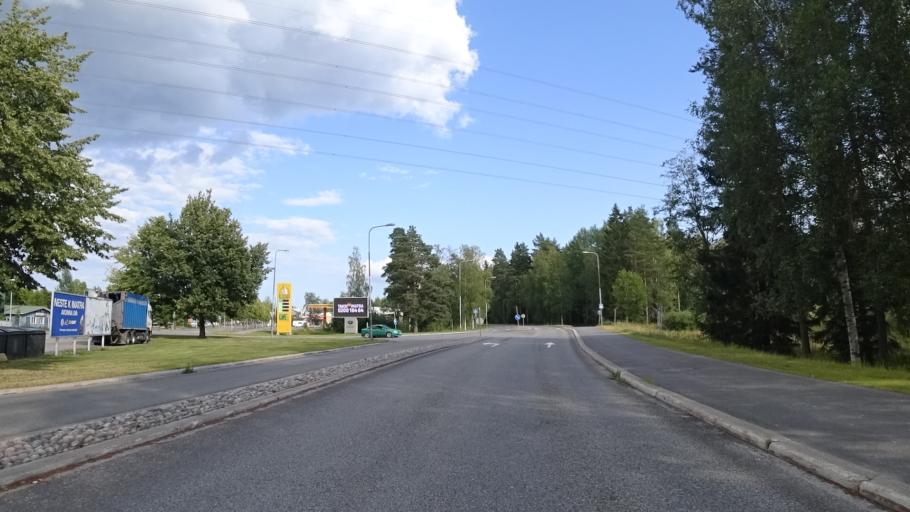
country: FI
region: South Karelia
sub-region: Imatra
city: Imatra
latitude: 61.1719
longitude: 28.7518
